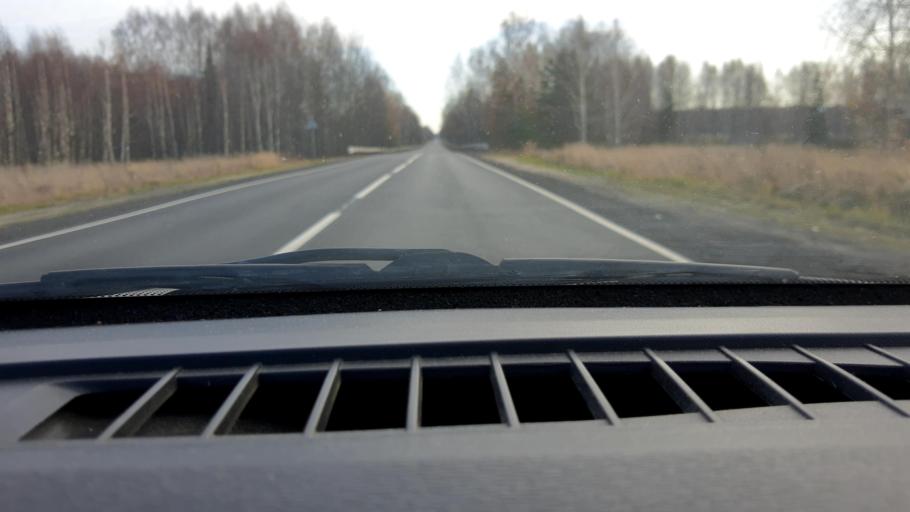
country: RU
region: Nizjnij Novgorod
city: Novaya Balakhna
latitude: 56.5691
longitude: 43.7132
